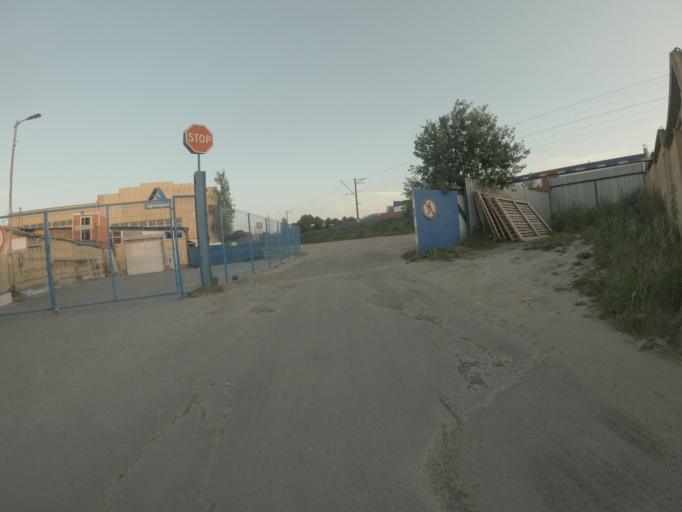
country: RU
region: St.-Petersburg
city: Krasnogvargeisky
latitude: 59.9435
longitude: 30.4482
